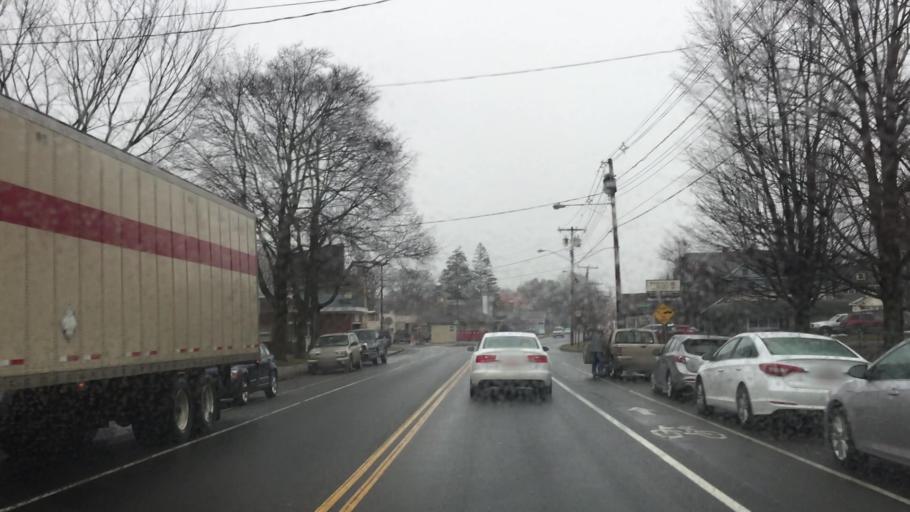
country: US
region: Massachusetts
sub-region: Berkshire County
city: Pittsfield
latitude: 42.4443
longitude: -73.2407
